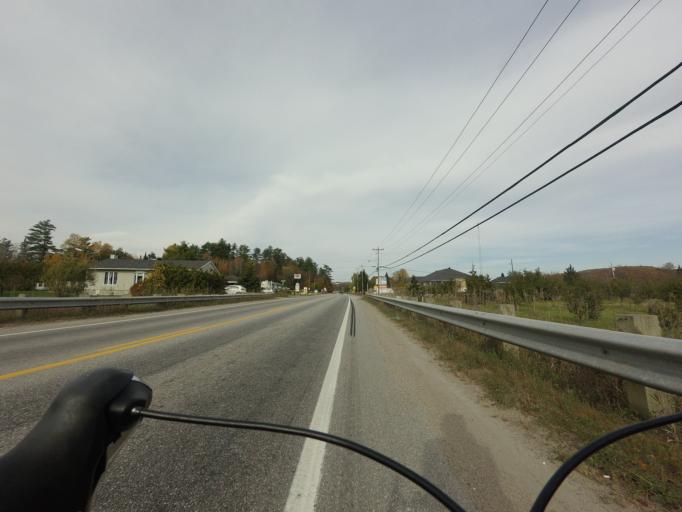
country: CA
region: Quebec
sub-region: Outaouais
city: Val-des-Monts
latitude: 45.5837
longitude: -75.6183
